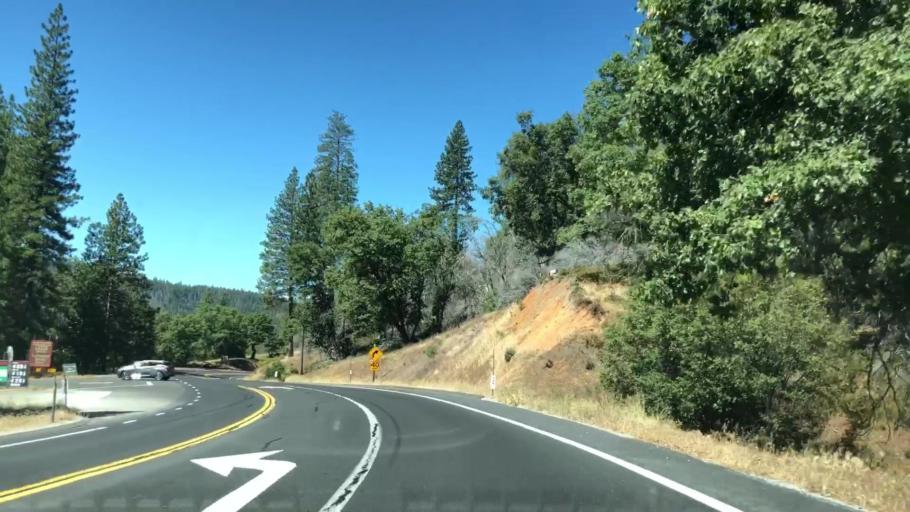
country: US
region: California
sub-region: Mariposa County
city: Midpines
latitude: 37.8165
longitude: -119.9388
